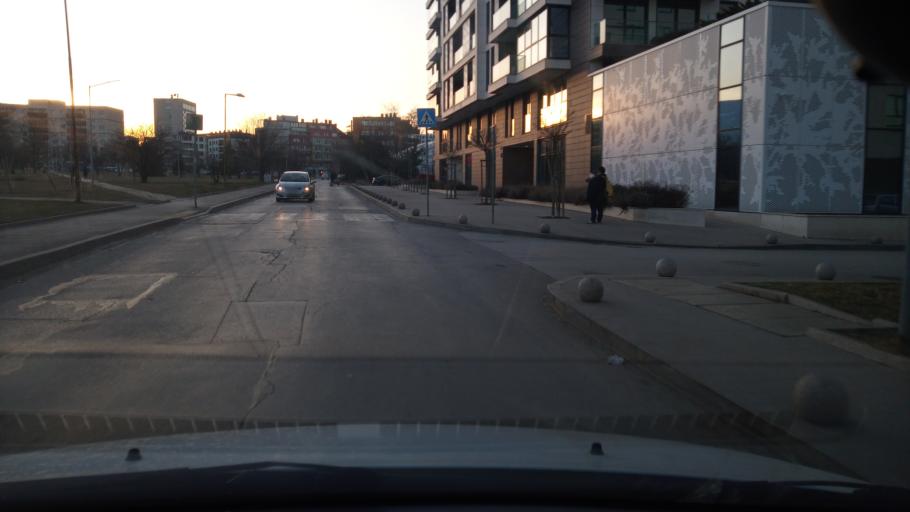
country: BG
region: Sofia-Capital
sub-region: Stolichna Obshtina
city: Sofia
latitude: 42.6566
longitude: 23.3528
